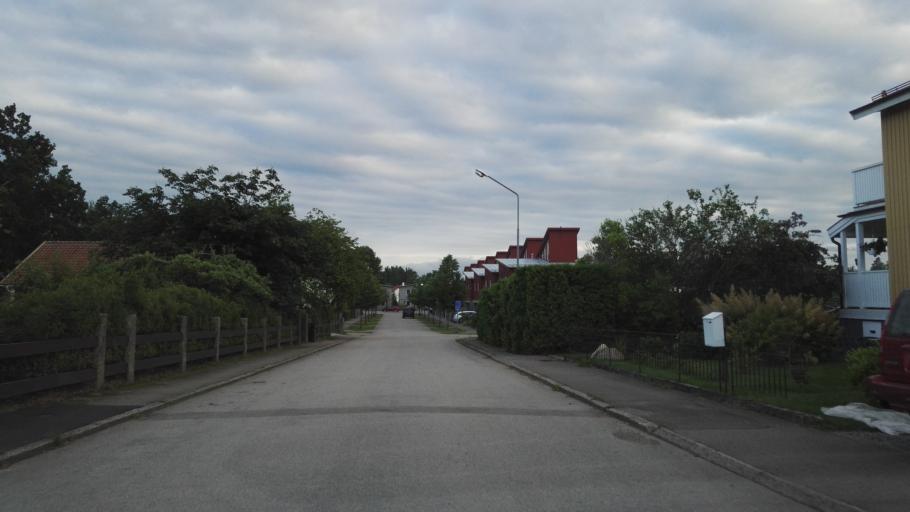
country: SE
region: Kronoberg
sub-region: Vaxjo Kommun
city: Vaexjoe
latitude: 56.8672
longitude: 14.8028
